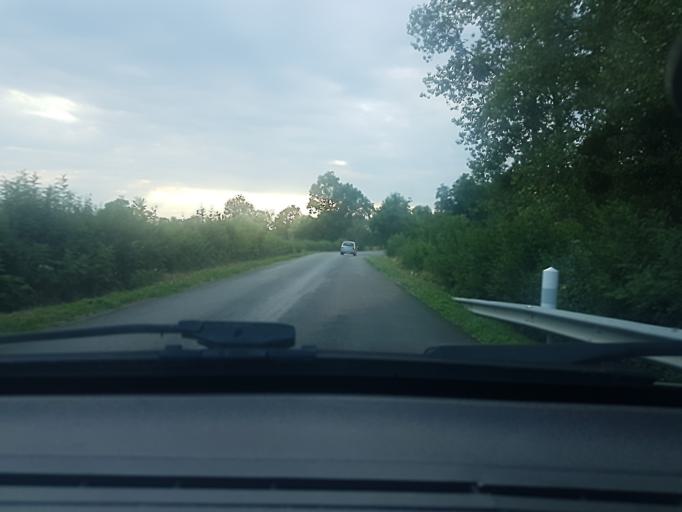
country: FR
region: Bourgogne
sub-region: Departement de Saone-et-Loire
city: Sennecey-le-Grand
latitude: 46.6688
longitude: 4.8192
